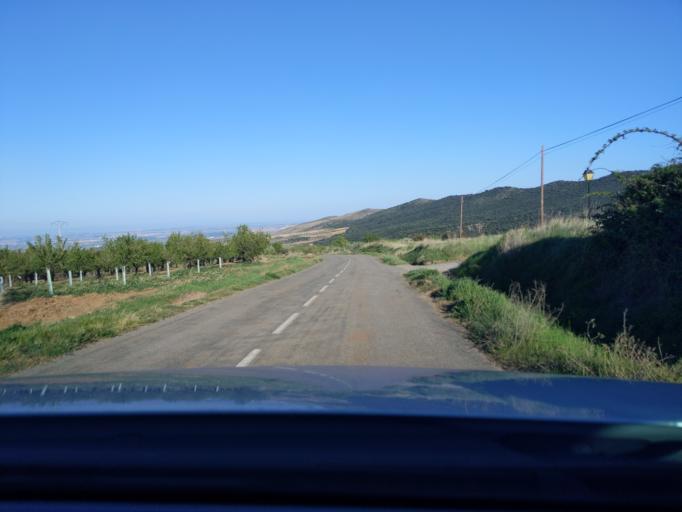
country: ES
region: La Rioja
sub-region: Provincia de La Rioja
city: Bergasillas Bajera
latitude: 42.2454
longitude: -2.1564
